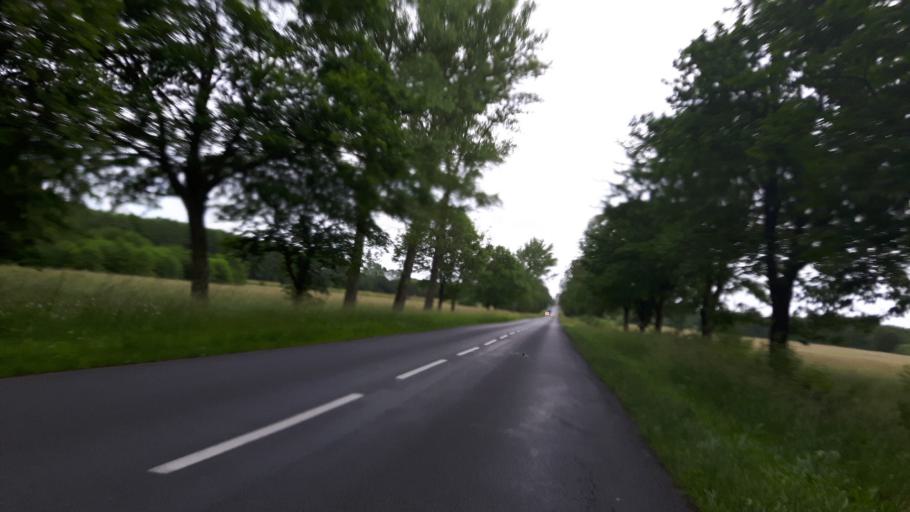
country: PL
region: West Pomeranian Voivodeship
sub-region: Powiat gryficki
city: Gryfice
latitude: 53.9642
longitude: 15.2299
